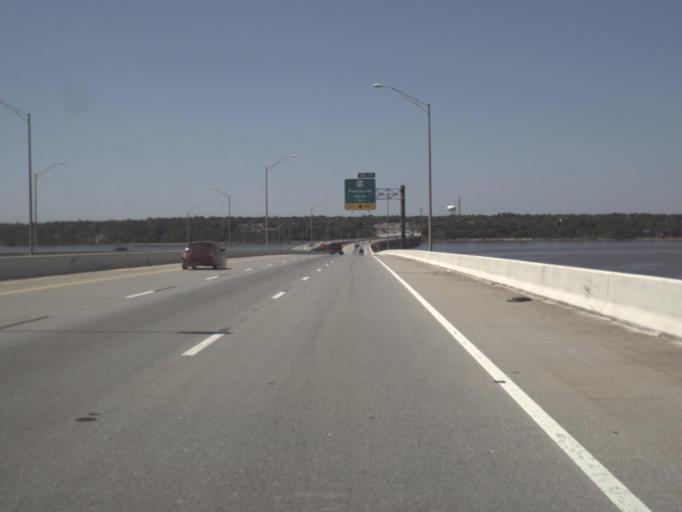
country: US
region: Florida
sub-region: Escambia County
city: Ferry Pass
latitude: 30.5154
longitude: -87.1495
